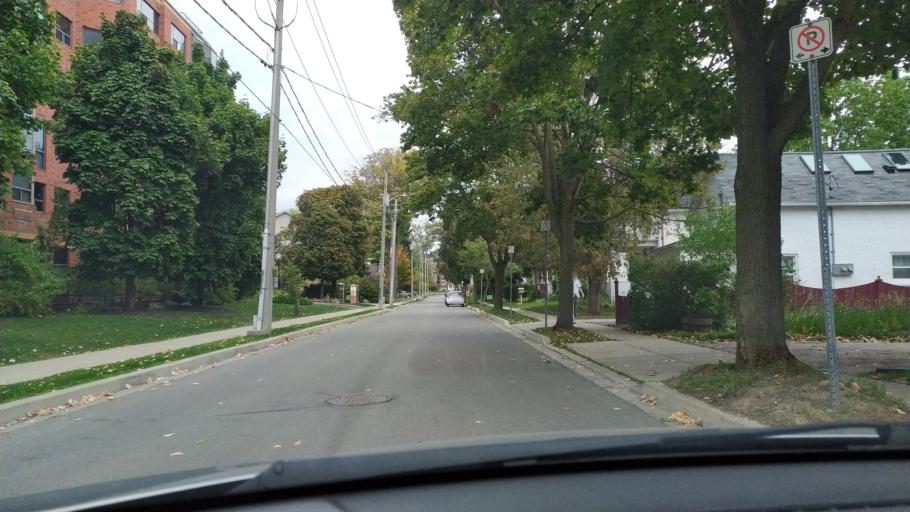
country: CA
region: Ontario
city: Waterloo
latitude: 43.4548
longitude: -80.4833
